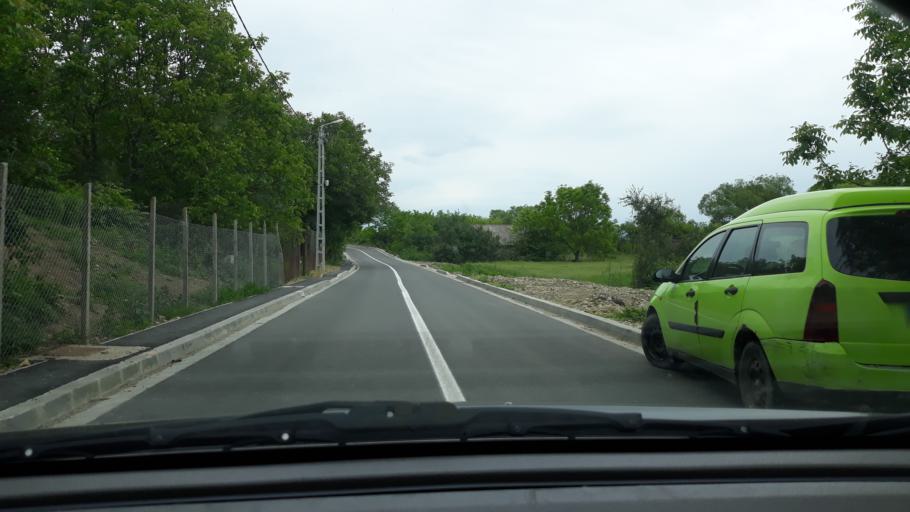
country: RO
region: Bihor
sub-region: Comuna Osorheiu
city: Osorheiu
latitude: 47.0617
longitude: 22.0282
